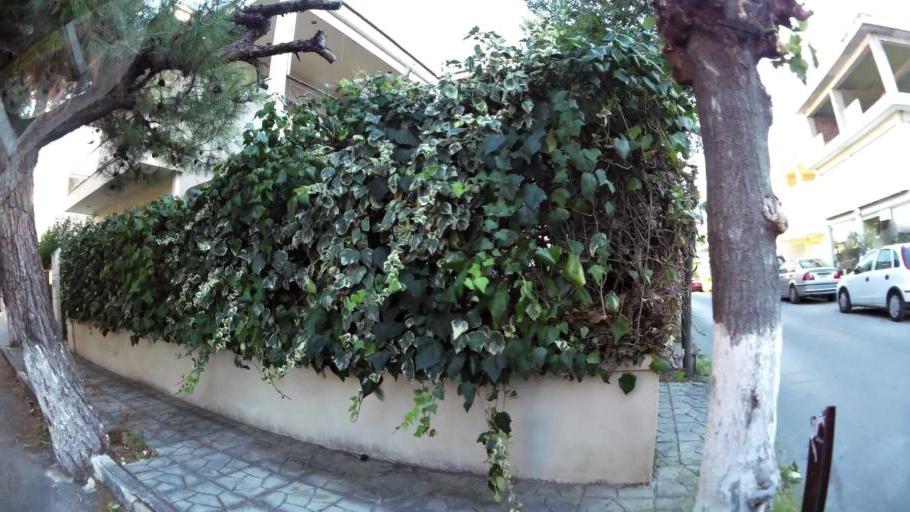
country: GR
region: Attica
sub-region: Nomarchia Athinas
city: Neo Psychiko
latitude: 38.0105
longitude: 23.7933
